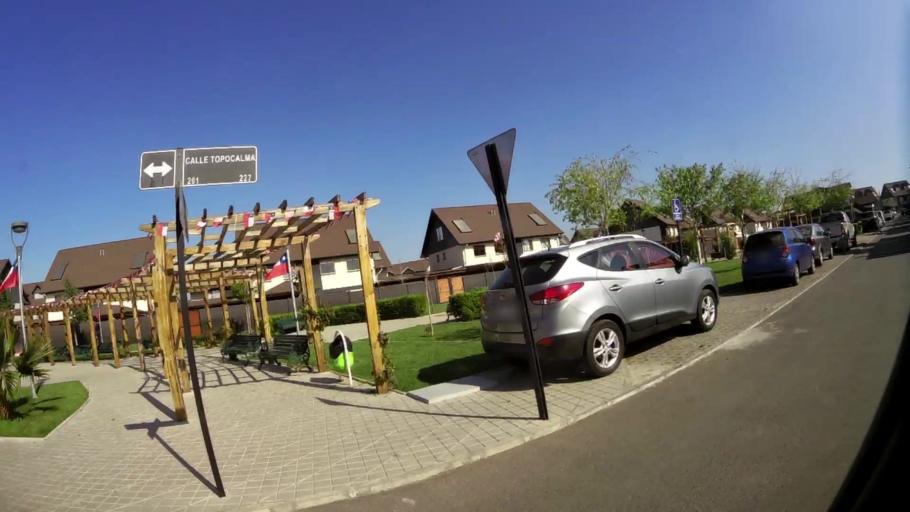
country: CL
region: Santiago Metropolitan
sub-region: Provincia de Santiago
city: Lo Prado
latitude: -33.4825
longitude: -70.7676
